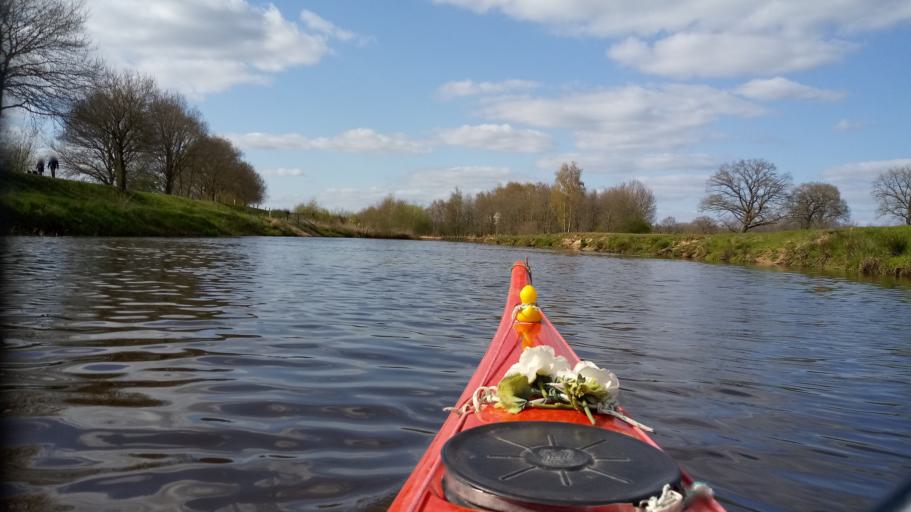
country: NL
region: Overijssel
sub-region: Gemeente Twenterand
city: Den Ham
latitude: 52.4935
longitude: 6.4172
